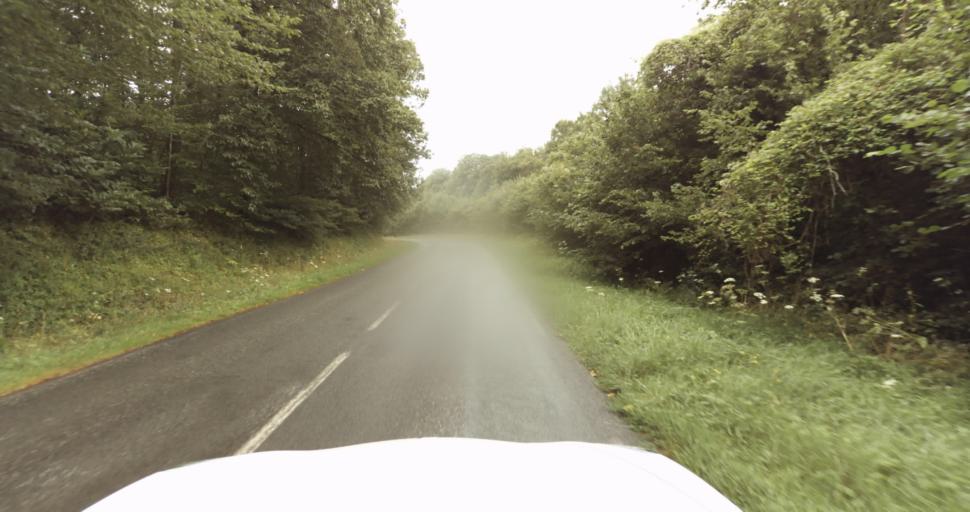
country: FR
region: Haute-Normandie
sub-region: Departement de l'Eure
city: Normanville
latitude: 49.0789
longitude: 1.1735
